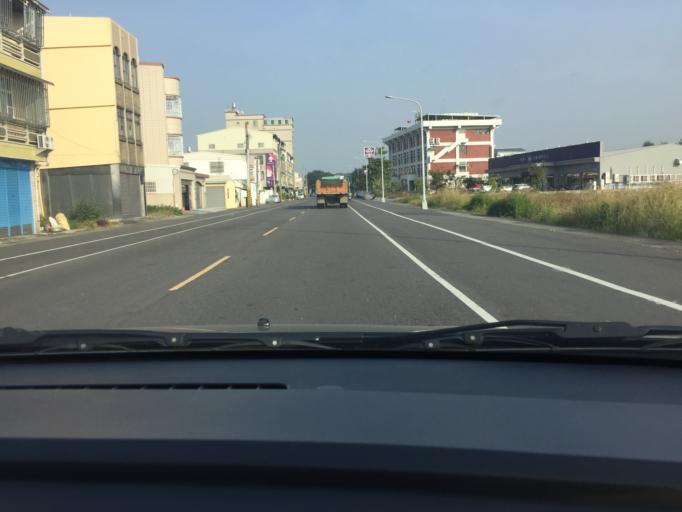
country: TW
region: Taiwan
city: Xinying
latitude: 23.1933
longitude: 120.3117
